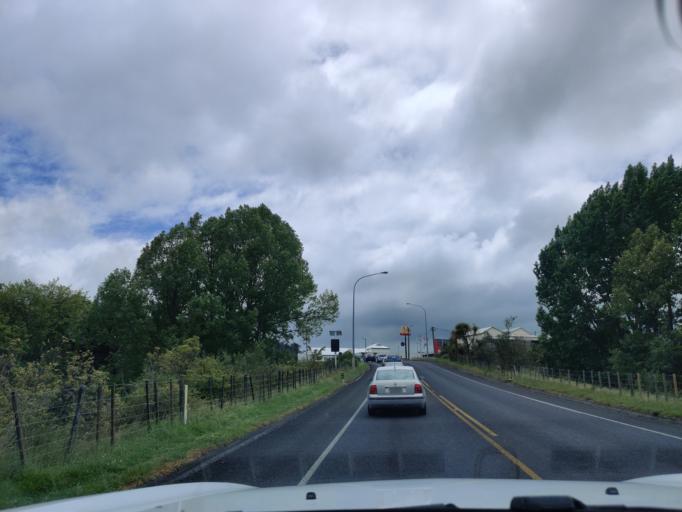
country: NZ
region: Manawatu-Wanganui
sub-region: Ruapehu District
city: Waiouru
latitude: -39.6810
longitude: 175.8006
